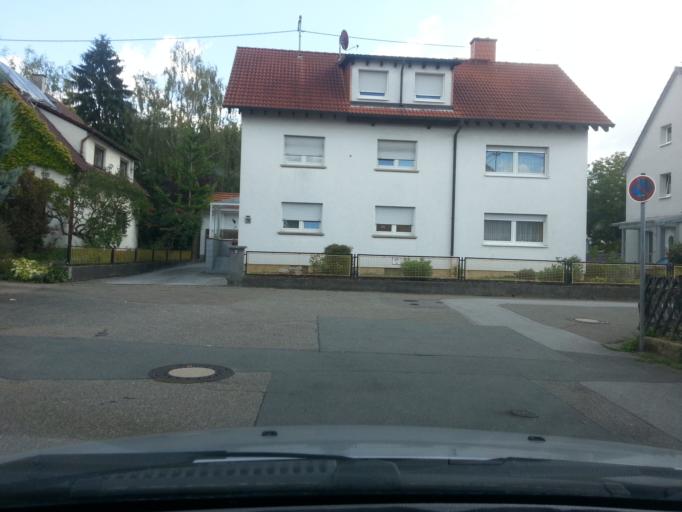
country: DE
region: Baden-Wuerttemberg
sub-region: Karlsruhe Region
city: Wiesloch
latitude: 49.2777
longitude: 8.6744
